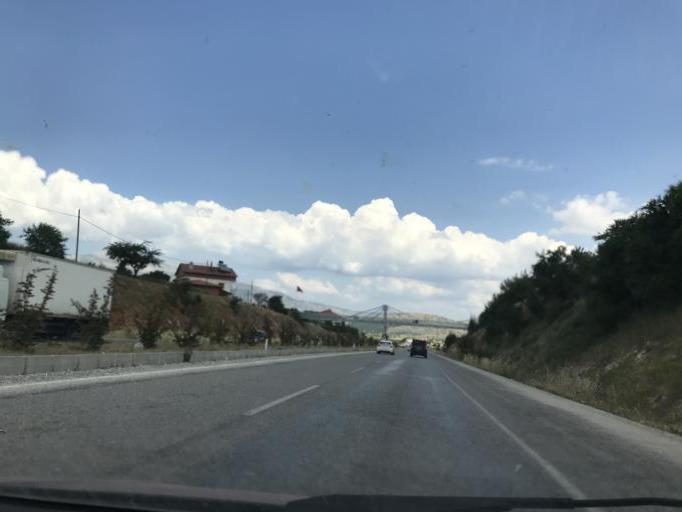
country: TR
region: Denizli
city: Serinhisar
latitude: 37.6157
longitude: 29.1692
